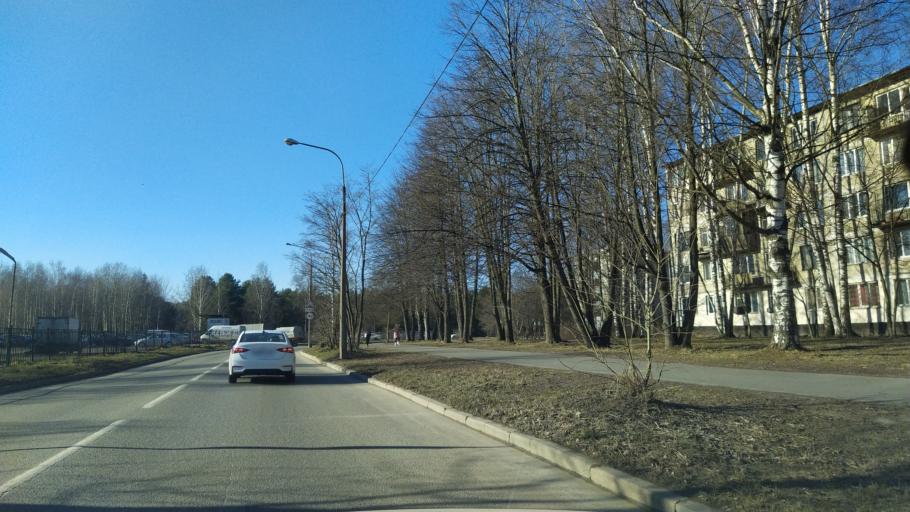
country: RU
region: Leningrad
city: Akademicheskoe
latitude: 60.0009
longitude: 30.4233
